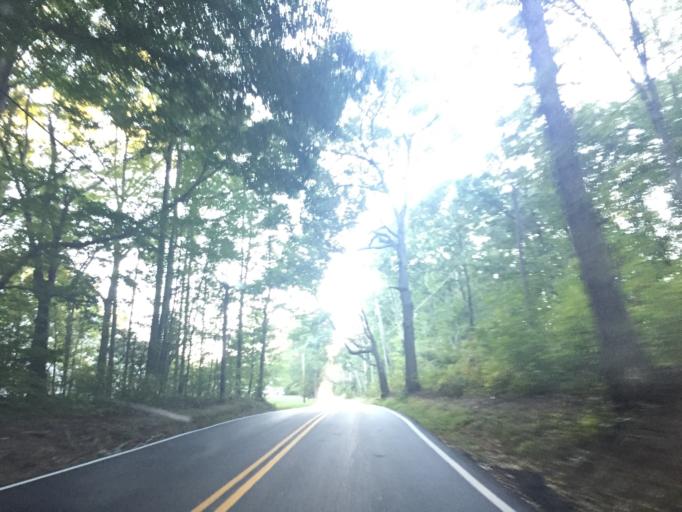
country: US
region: Maryland
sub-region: Harford County
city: Joppatowne
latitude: 39.4674
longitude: -76.3595
